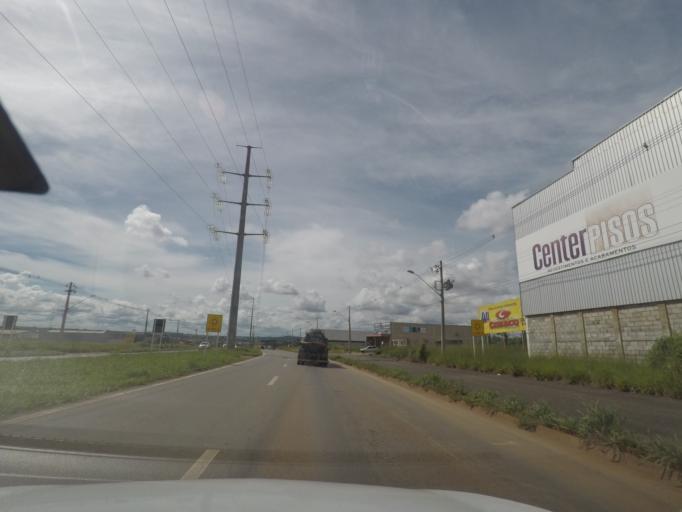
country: BR
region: Goias
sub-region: Goiania
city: Goiania
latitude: -16.7273
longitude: -49.3510
